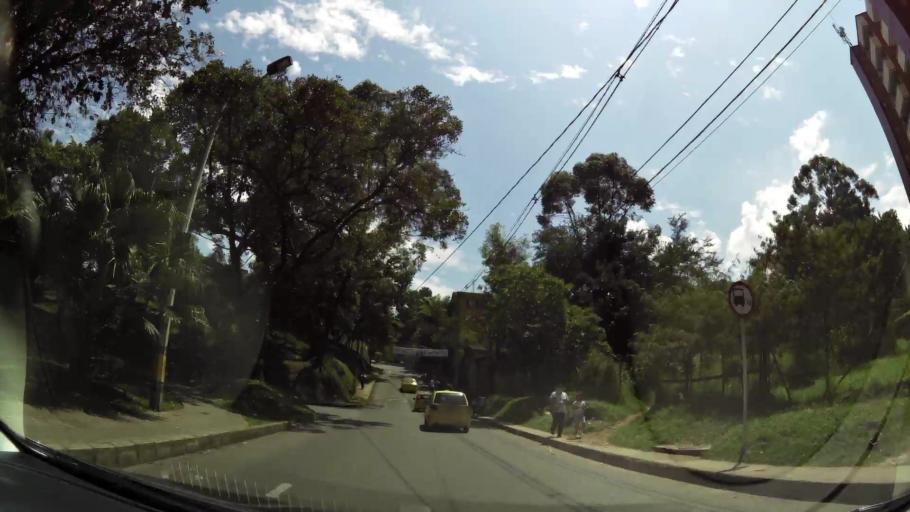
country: CO
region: Antioquia
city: Itagui
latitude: 6.2219
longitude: -75.6087
